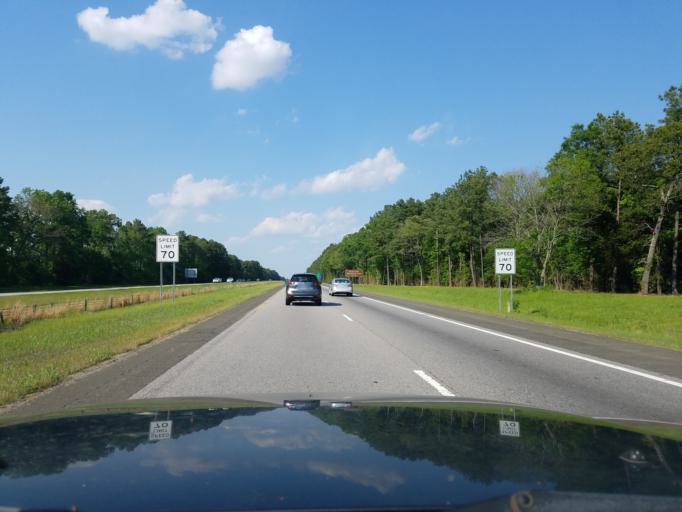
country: US
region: North Carolina
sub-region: Granville County
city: Butner
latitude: 36.1297
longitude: -78.7397
